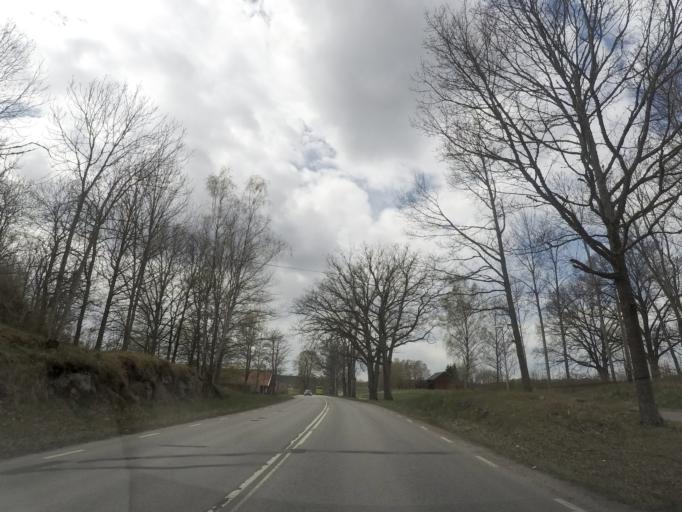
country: SE
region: Soedermanland
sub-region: Nykopings Kommun
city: Nykoping
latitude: 58.7460
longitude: 16.9693
